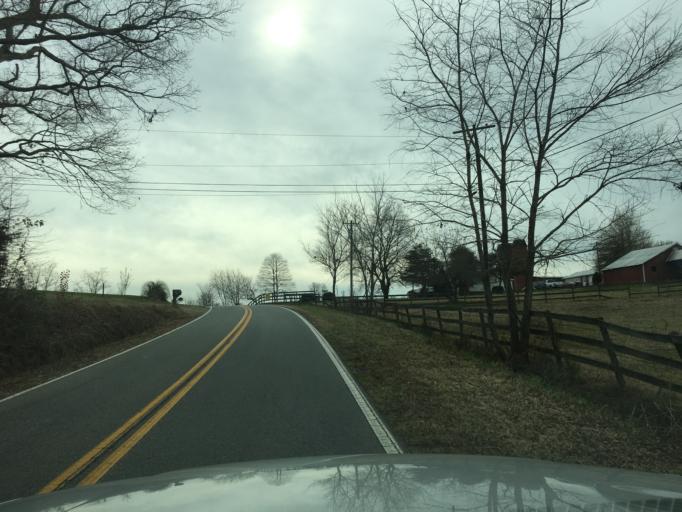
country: US
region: North Carolina
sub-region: McDowell County
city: West Marion
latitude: 35.6279
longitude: -81.9666
